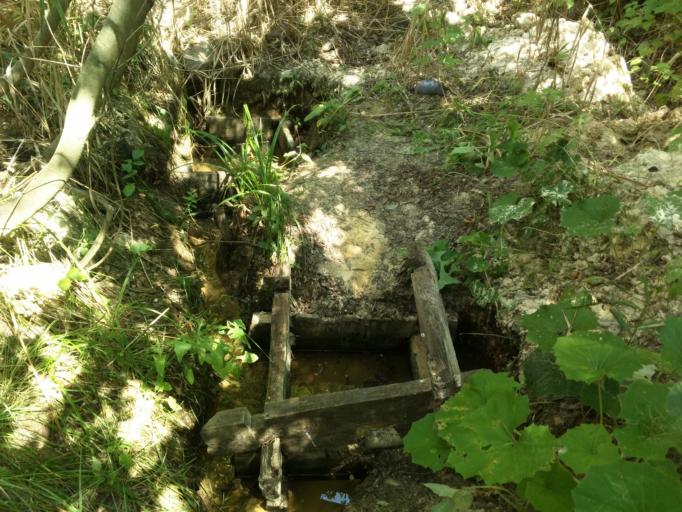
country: RU
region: Voronezj
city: Kalach
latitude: 50.4786
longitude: 41.0733
